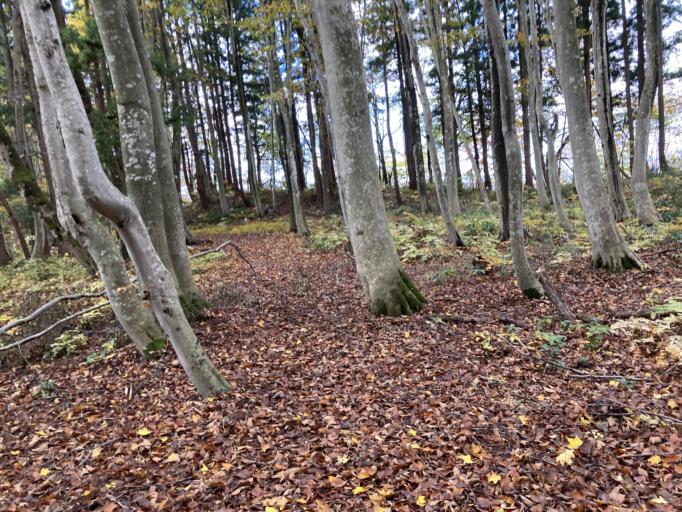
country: JP
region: Niigata
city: Tokamachi
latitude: 37.1538
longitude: 138.6273
